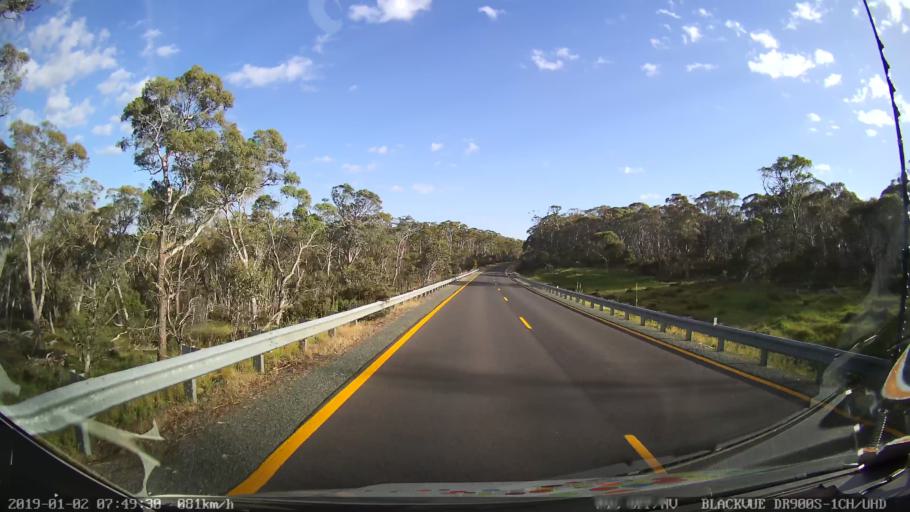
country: AU
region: New South Wales
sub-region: Tumut Shire
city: Tumut
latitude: -35.7409
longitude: 148.5225
